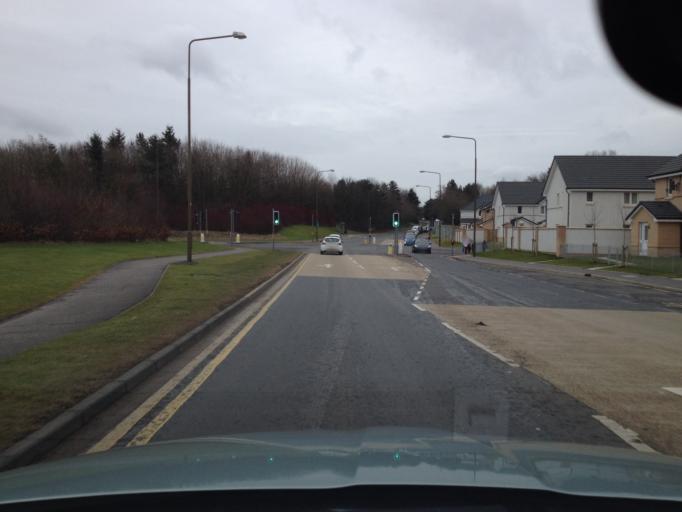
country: GB
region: Scotland
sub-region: West Lothian
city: Livingston
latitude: 55.8864
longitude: -3.5261
